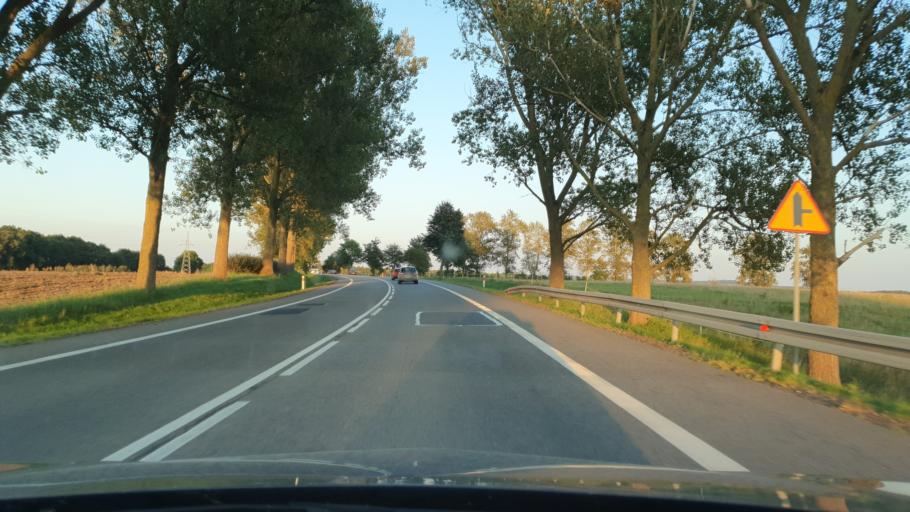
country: PL
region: Pomeranian Voivodeship
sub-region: Powiat slupski
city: Potegowo
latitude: 54.4785
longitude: 17.5371
